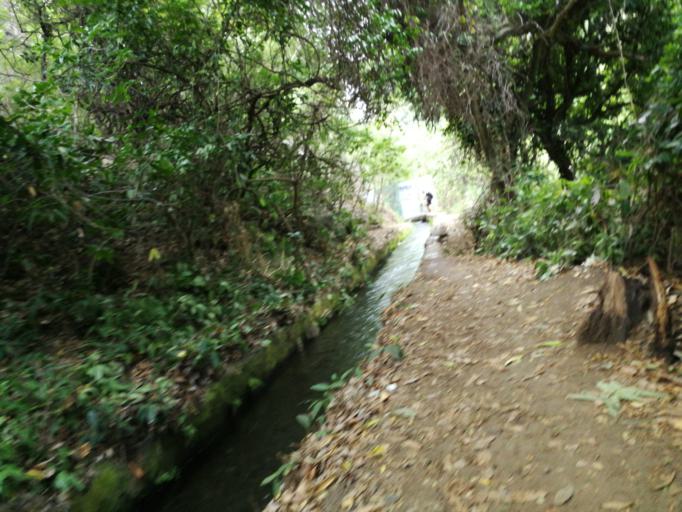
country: RE
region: Reunion
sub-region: Reunion
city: Saint-Paul
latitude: -21.0455
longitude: 55.2456
